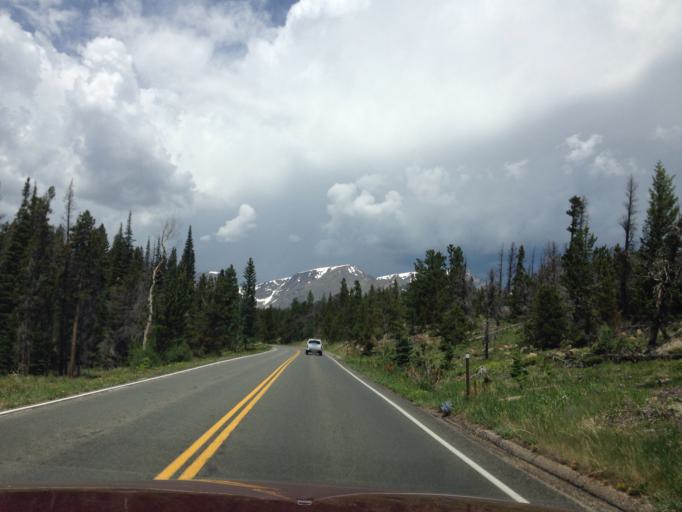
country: US
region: Colorado
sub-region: Larimer County
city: Estes Park
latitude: 40.3954
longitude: -105.6324
